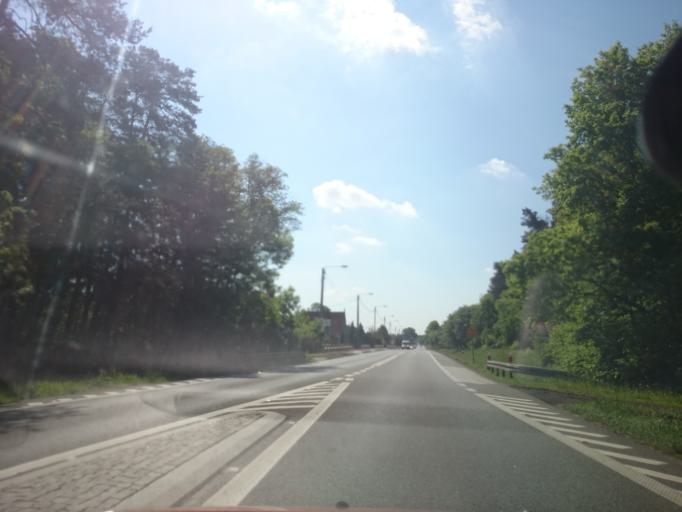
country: PL
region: Opole Voivodeship
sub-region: Powiat opolski
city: Tarnow Opolski
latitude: 50.6127
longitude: 18.0677
